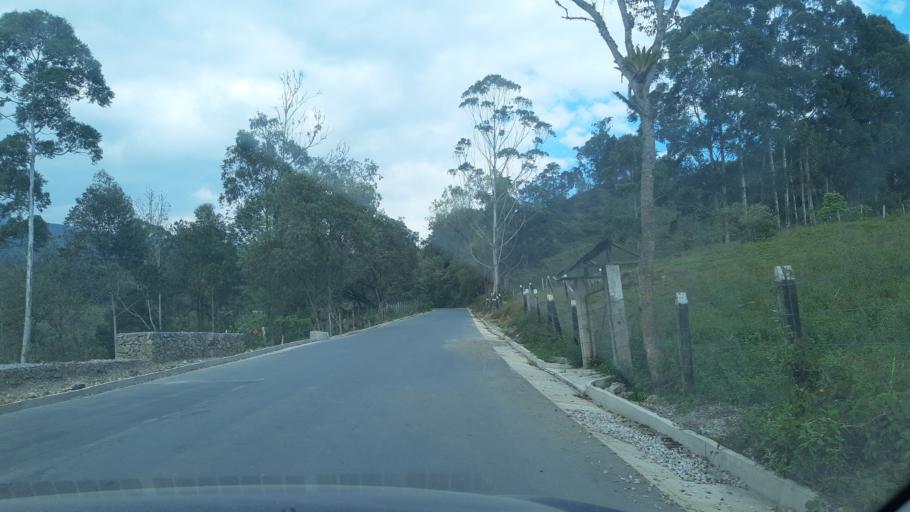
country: CO
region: Boyaca
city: Garagoa
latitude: 5.0884
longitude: -73.3490
